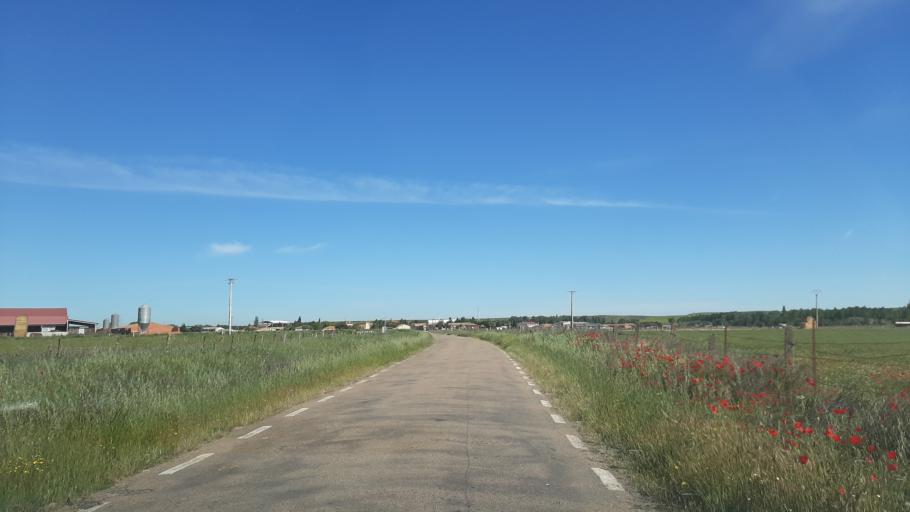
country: ES
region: Castille and Leon
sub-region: Provincia de Salamanca
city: Pedrosillo de Alba
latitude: 40.8167
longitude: -5.3897
